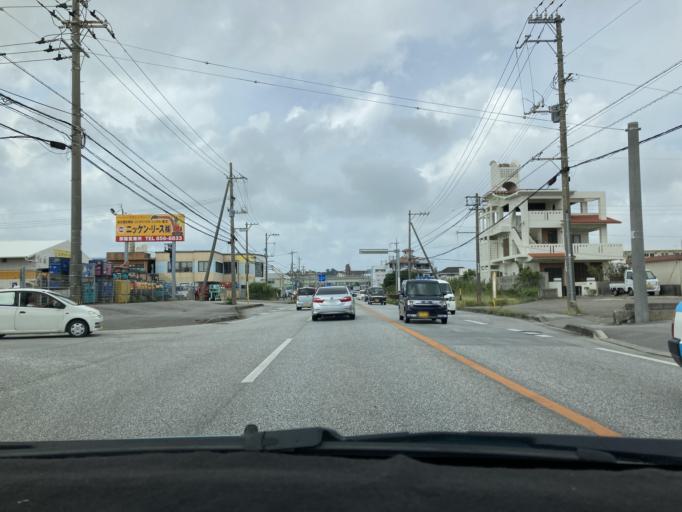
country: JP
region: Okinawa
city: Tomigusuku
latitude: 26.1710
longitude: 127.6669
